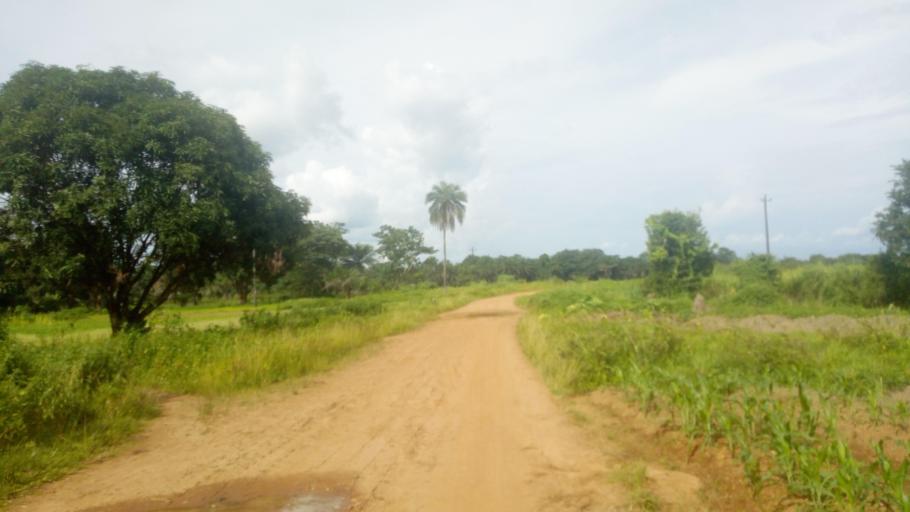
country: SL
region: Northern Province
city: Magburaka
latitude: 8.6766
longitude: -12.0088
